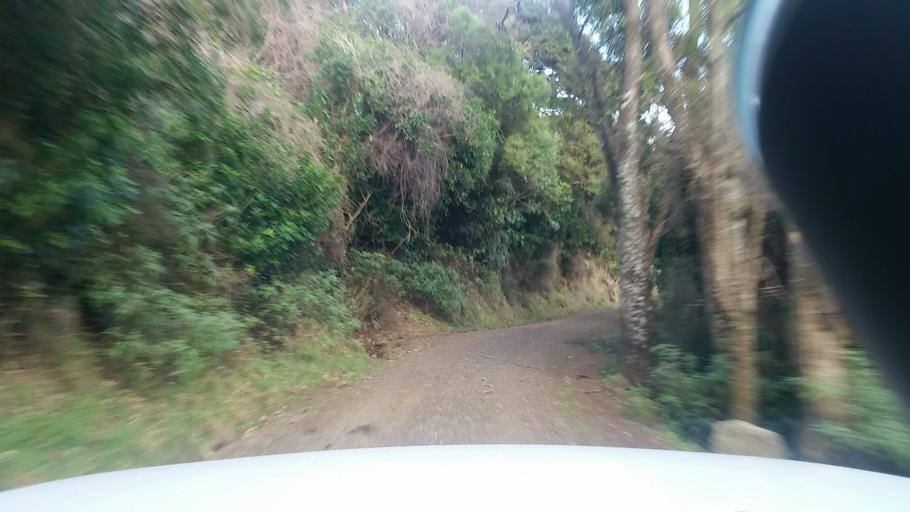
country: NZ
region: Canterbury
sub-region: Christchurch City
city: Christchurch
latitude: -43.7568
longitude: 172.9986
